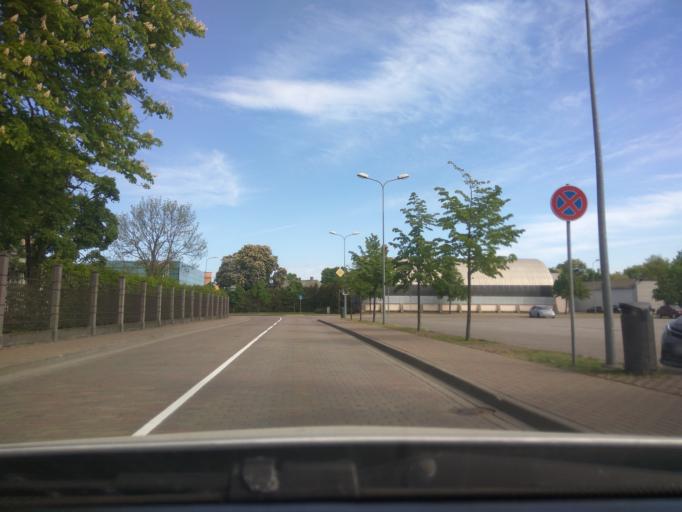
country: LV
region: Ventspils
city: Ventspils
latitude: 57.3971
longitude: 21.5708
